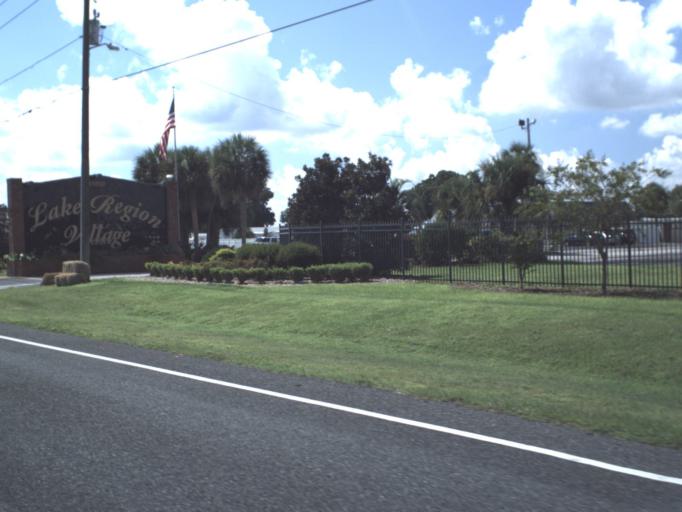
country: US
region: Florida
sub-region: Polk County
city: Lake Hamilton
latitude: 28.0674
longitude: -81.6421
